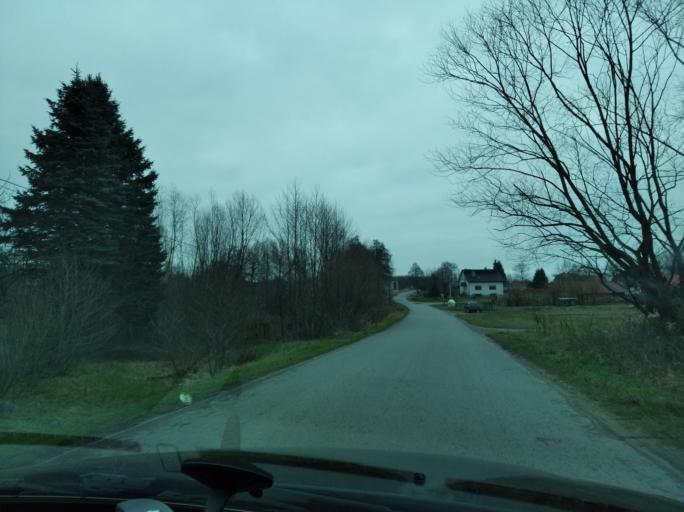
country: PL
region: Subcarpathian Voivodeship
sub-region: Powiat lancucki
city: Brzoza Stadnicka
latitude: 50.2056
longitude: 22.2972
